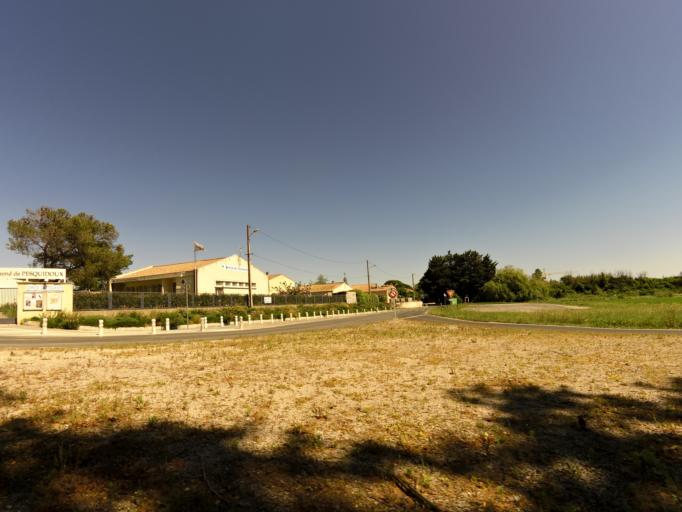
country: FR
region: Languedoc-Roussillon
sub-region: Departement de l'Herault
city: Castries
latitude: 43.6734
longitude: 3.9820
